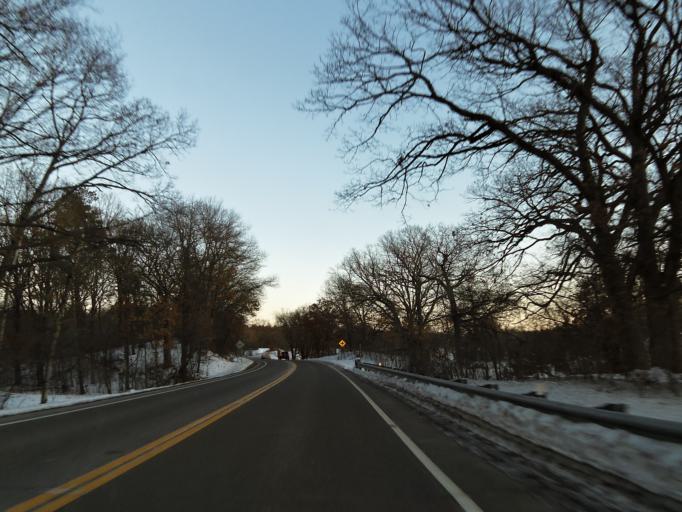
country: US
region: Minnesota
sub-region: Washington County
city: Dellwood
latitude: 45.0895
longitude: -92.9573
